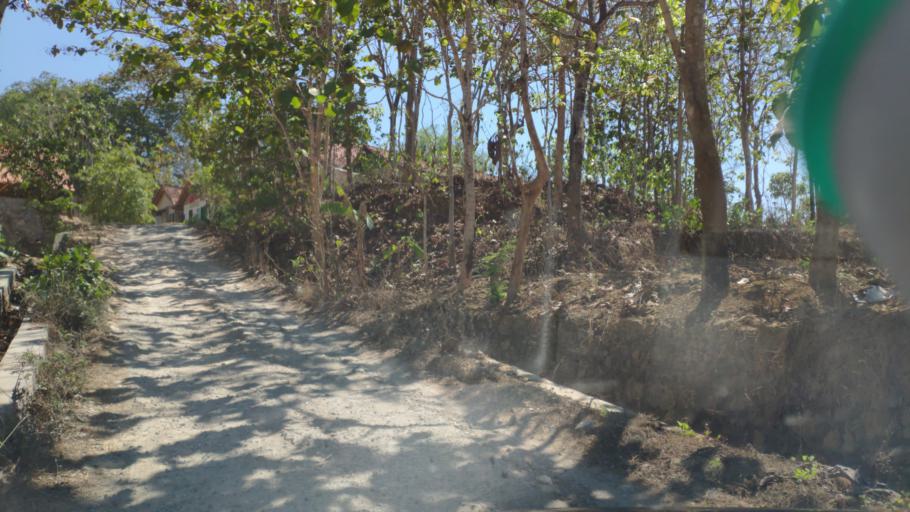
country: ID
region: Central Java
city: Jurangjero
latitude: -6.9047
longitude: 111.5064
